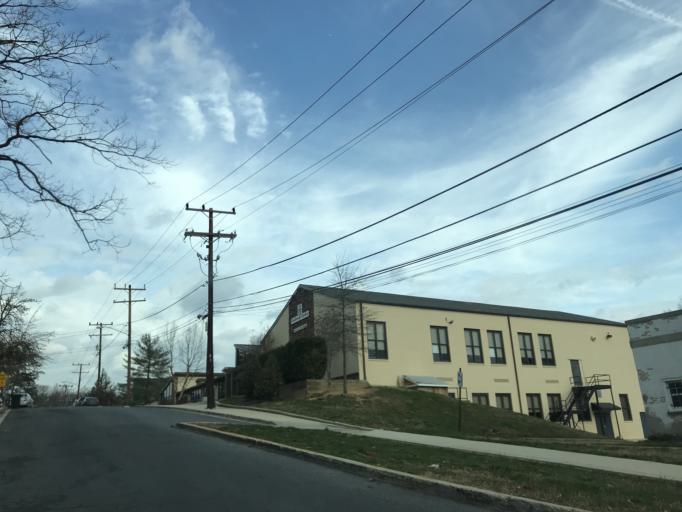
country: US
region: Maryland
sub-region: Prince George's County
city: Chillum
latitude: 38.9765
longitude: -76.9902
